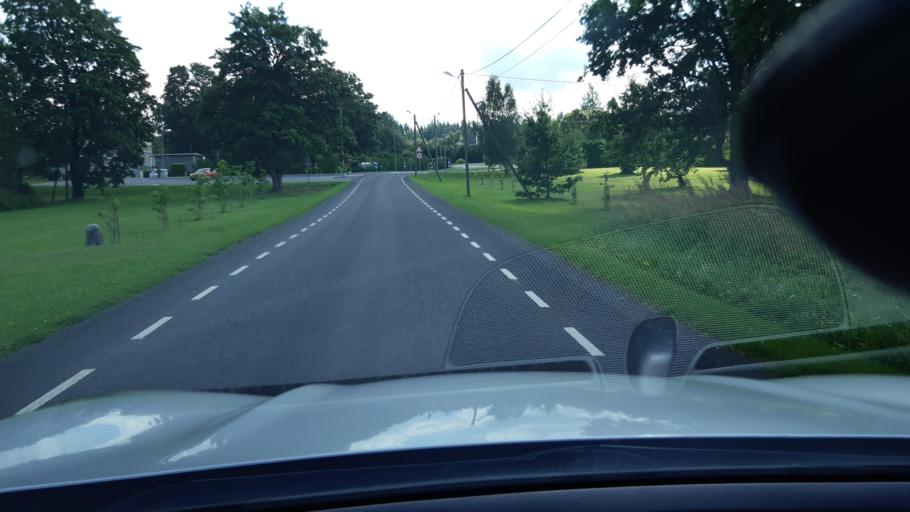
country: EE
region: Raplamaa
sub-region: Kehtna vald
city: Kehtna
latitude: 58.9431
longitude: 24.8973
